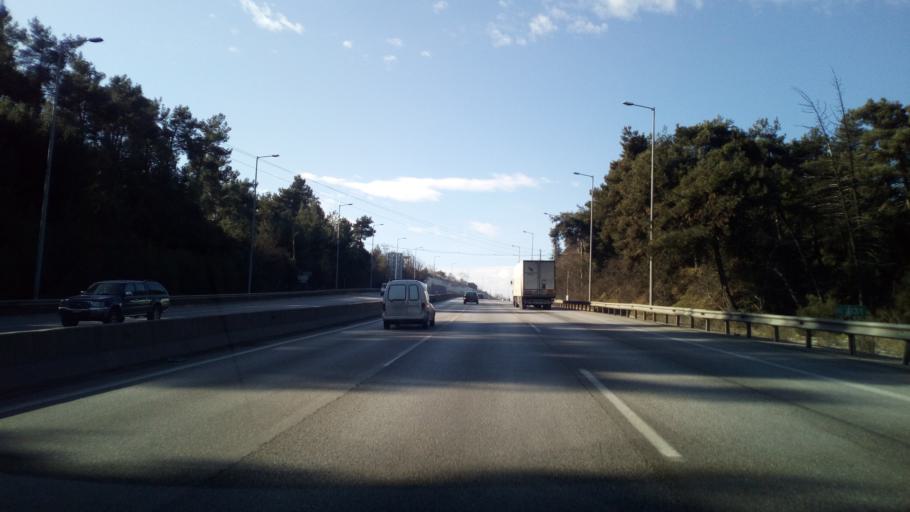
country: GR
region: Central Macedonia
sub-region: Nomos Thessalonikis
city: Liti
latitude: 40.7257
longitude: 22.9810
